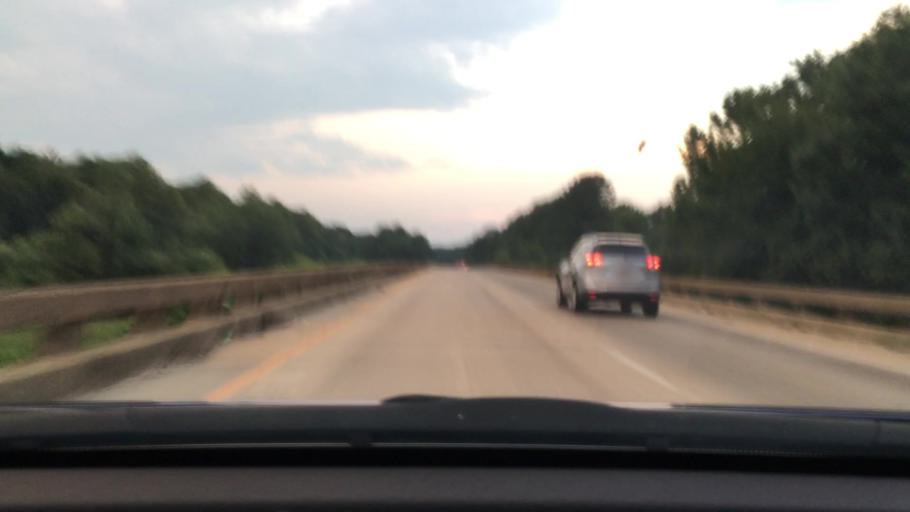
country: US
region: South Carolina
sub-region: Sumter County
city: Stateburg
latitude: 33.9478
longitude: -80.6266
